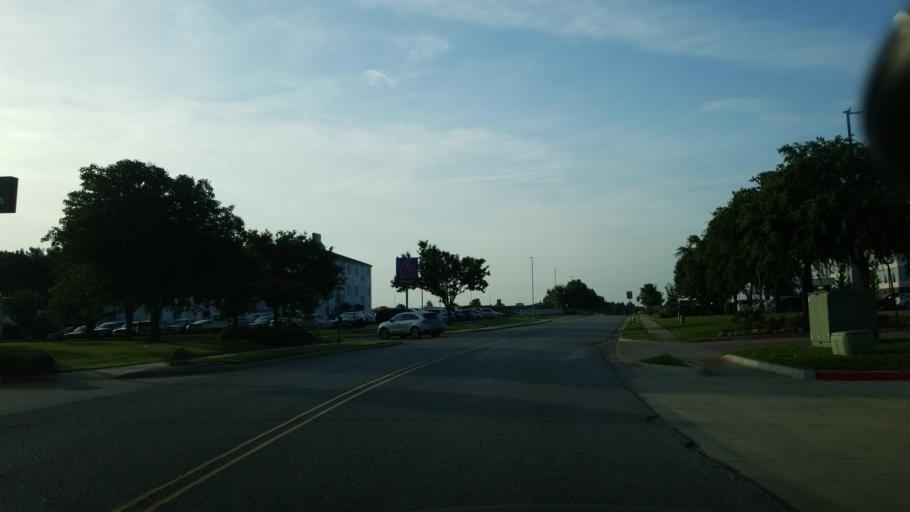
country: US
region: Texas
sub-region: Dallas County
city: Coppell
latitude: 32.9159
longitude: -97.0148
